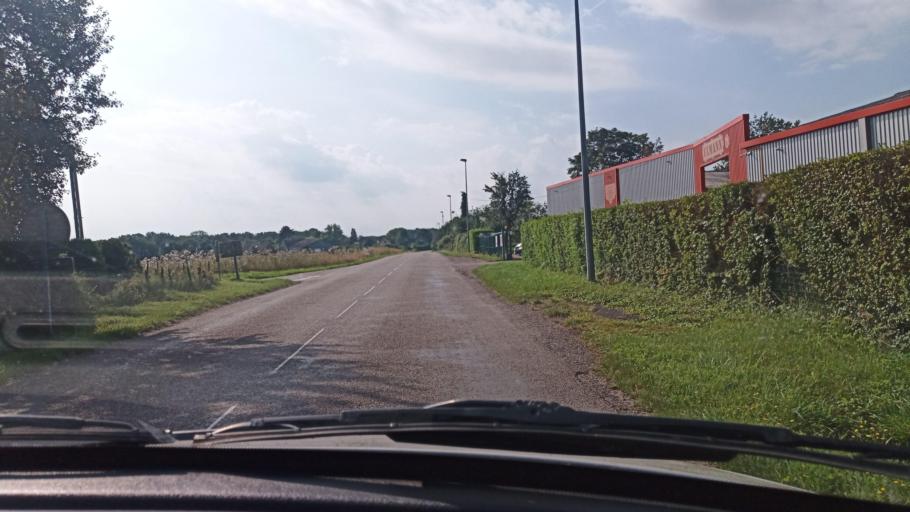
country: FR
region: Bourgogne
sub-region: Departement de l'Yonne
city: Saint-Valerien
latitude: 48.1940
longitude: 3.0882
